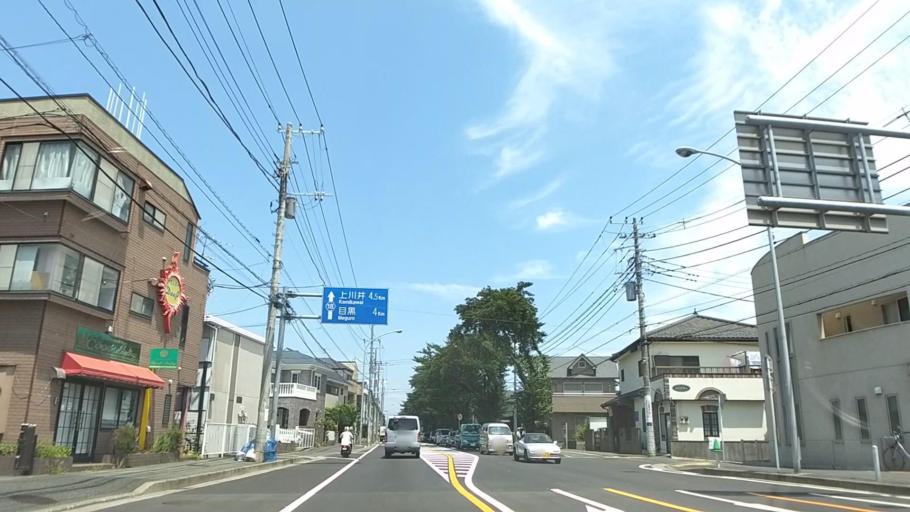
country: JP
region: Kanagawa
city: Minami-rinkan
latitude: 35.4728
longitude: 139.4807
